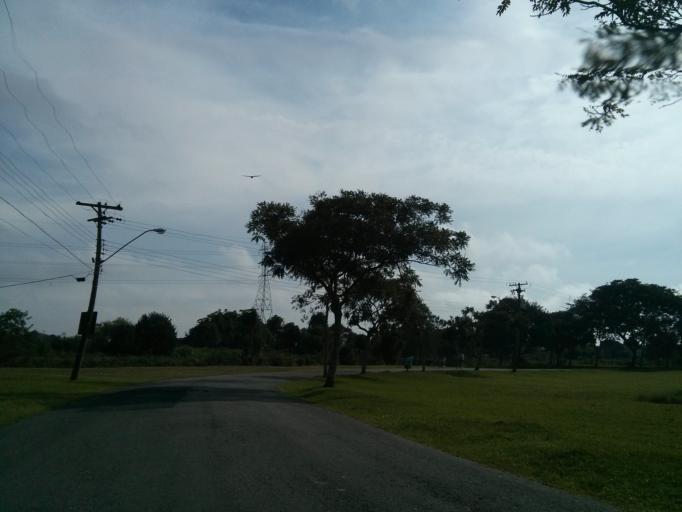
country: BR
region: Parana
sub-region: Sao Jose Dos Pinhais
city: Sao Jose dos Pinhais
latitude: -25.5198
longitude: -49.2217
